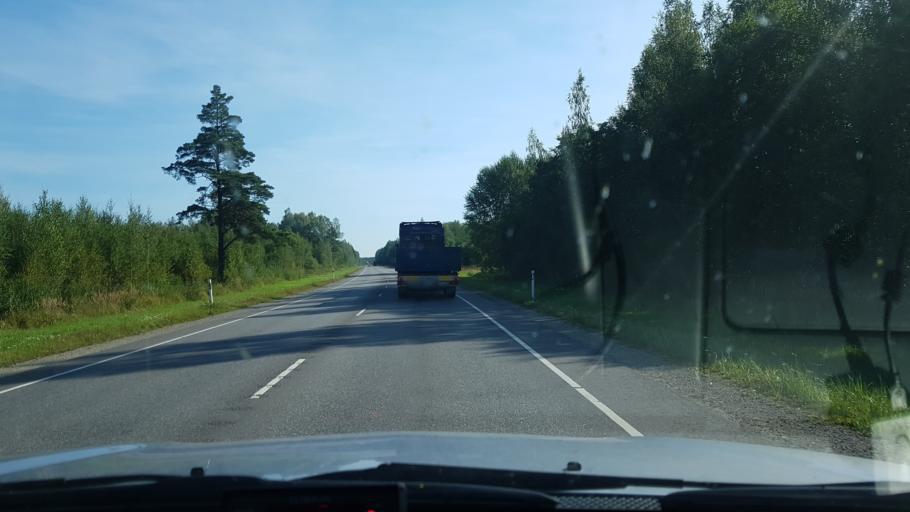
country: EE
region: Ida-Virumaa
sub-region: Toila vald
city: Toila
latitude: 59.3750
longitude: 27.5265
